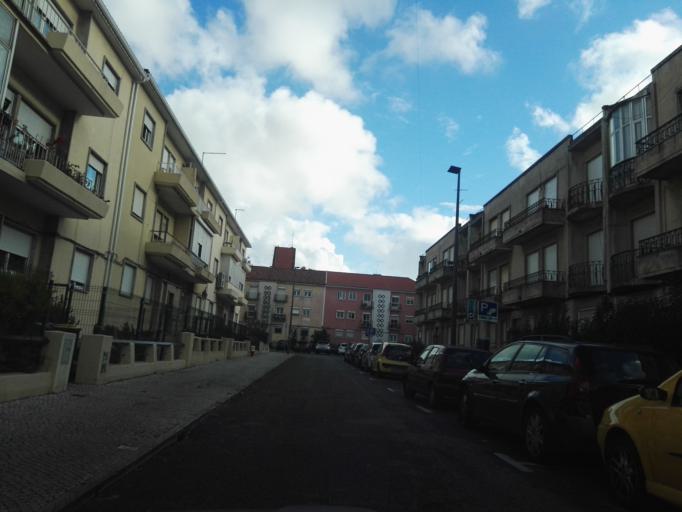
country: PT
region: Lisbon
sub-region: Lisbon
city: Lisbon
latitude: 38.7566
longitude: -9.1389
